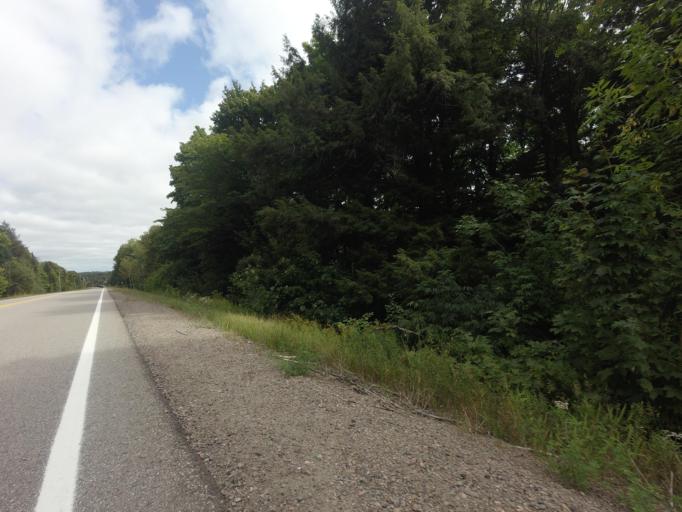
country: CA
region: Ontario
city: Omemee
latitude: 44.8931
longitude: -78.4749
